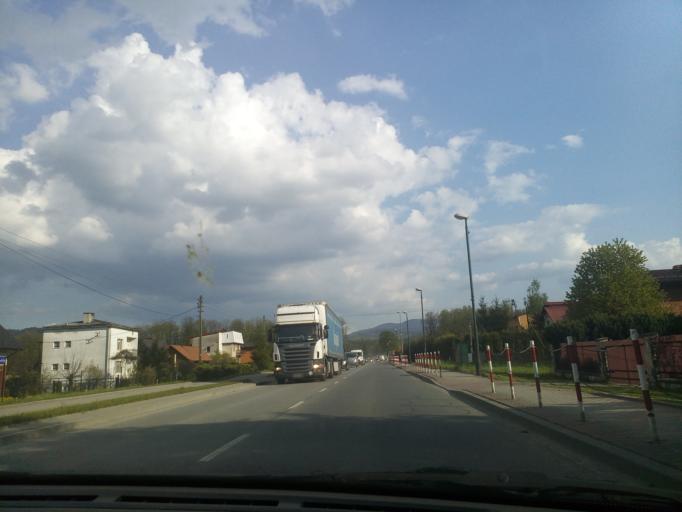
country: PL
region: Lesser Poland Voivodeship
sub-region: Powiat nowosadecki
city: Nawojowa
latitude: 49.5687
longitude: 20.7379
